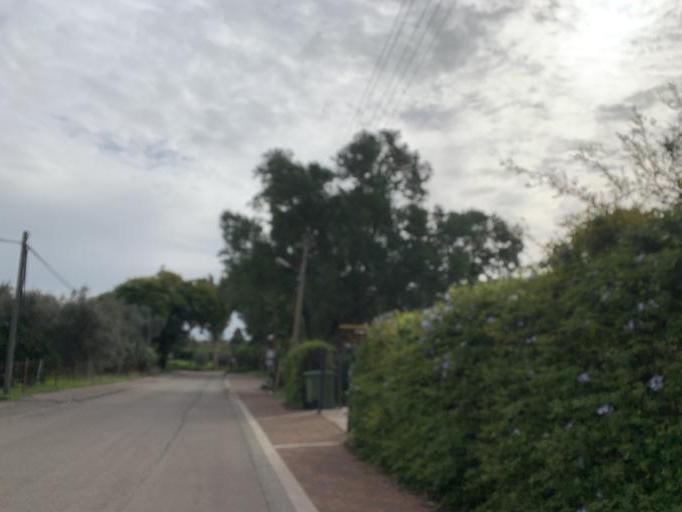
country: IL
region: Central District
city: Hod HaSharon
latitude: 32.1503
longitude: 34.8998
